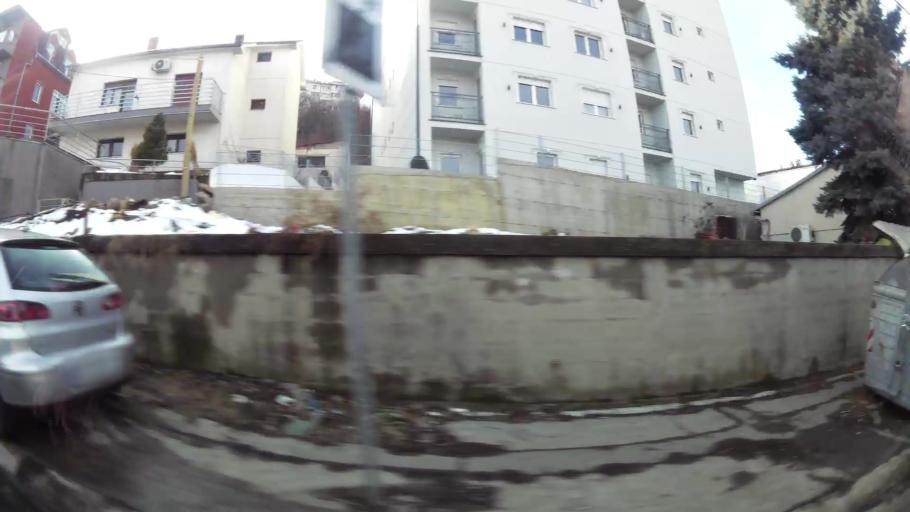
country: RS
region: Central Serbia
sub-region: Belgrade
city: Rakovica
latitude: 44.7311
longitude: 20.4277
